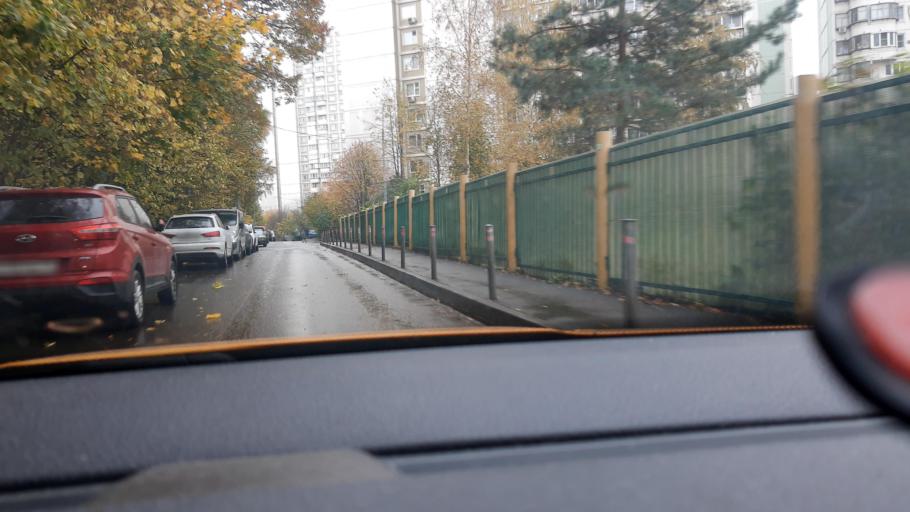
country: RU
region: Moskovskaya
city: Krasnogorsk
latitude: 55.8447
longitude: 37.3444
